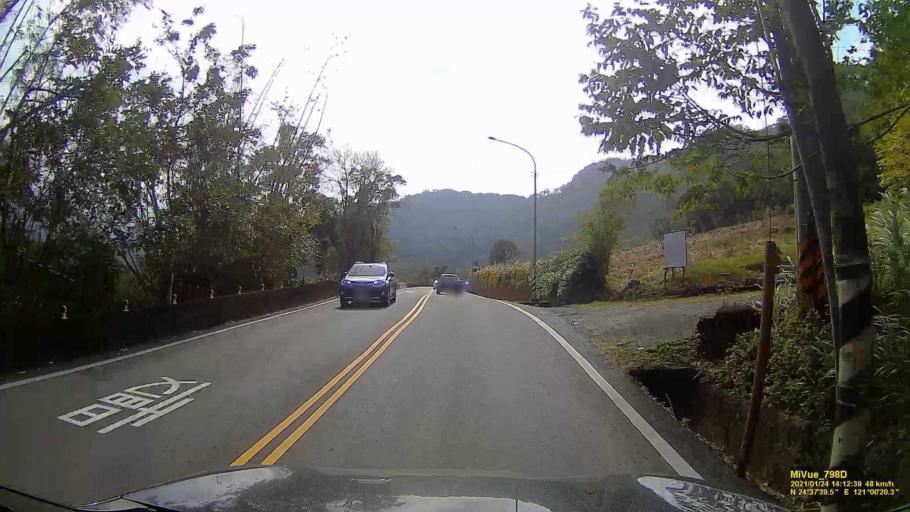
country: TW
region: Taiwan
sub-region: Hsinchu
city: Hsinchu
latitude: 24.6273
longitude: 121.0054
